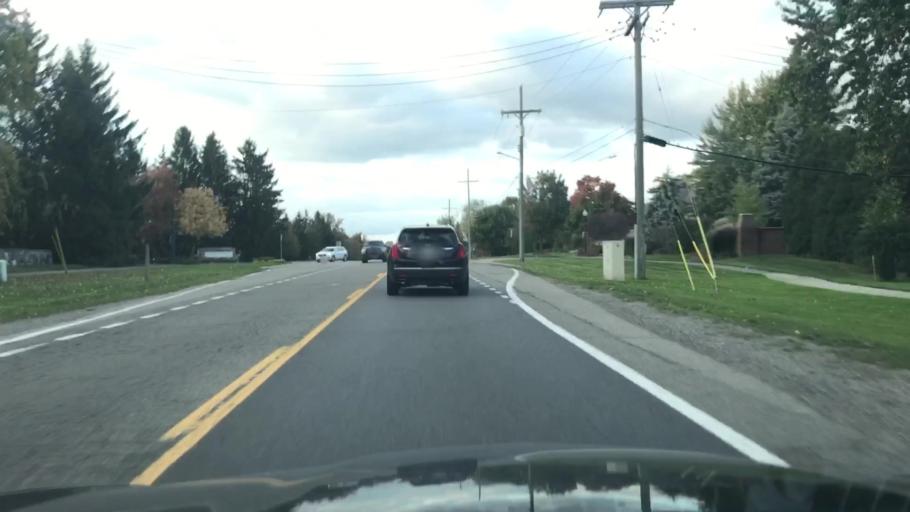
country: US
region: Michigan
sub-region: Oakland County
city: Rochester
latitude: 42.6868
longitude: -83.0943
